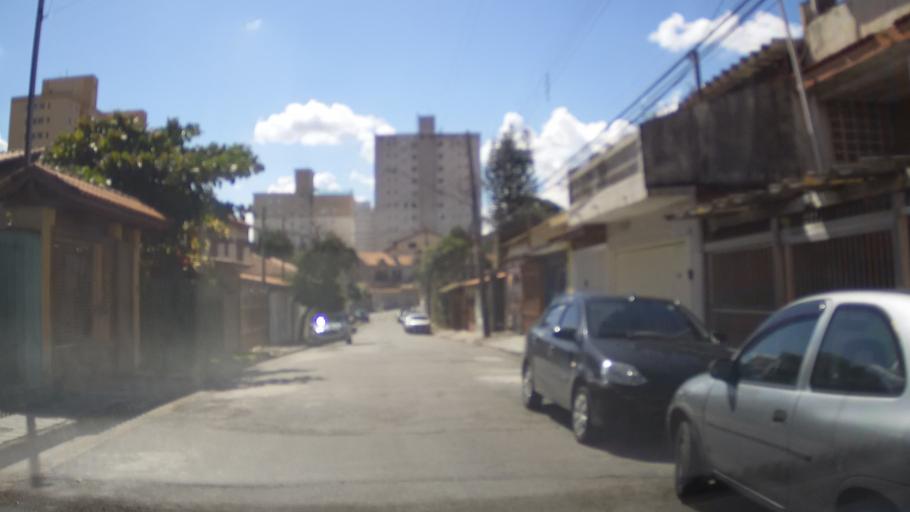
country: BR
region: Sao Paulo
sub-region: Guarulhos
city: Guarulhos
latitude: -23.4545
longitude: -46.5482
